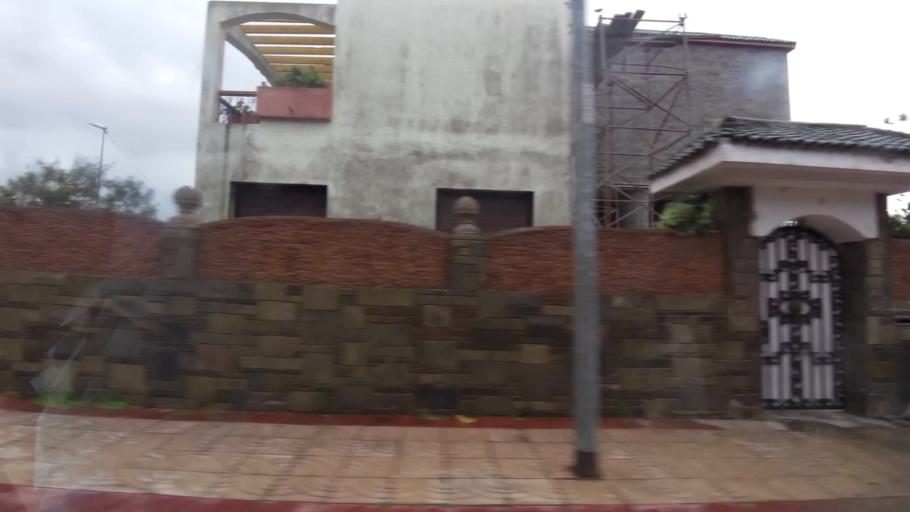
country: MA
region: Grand Casablanca
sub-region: Casablanca
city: Casablanca
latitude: 33.5783
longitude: -7.6773
